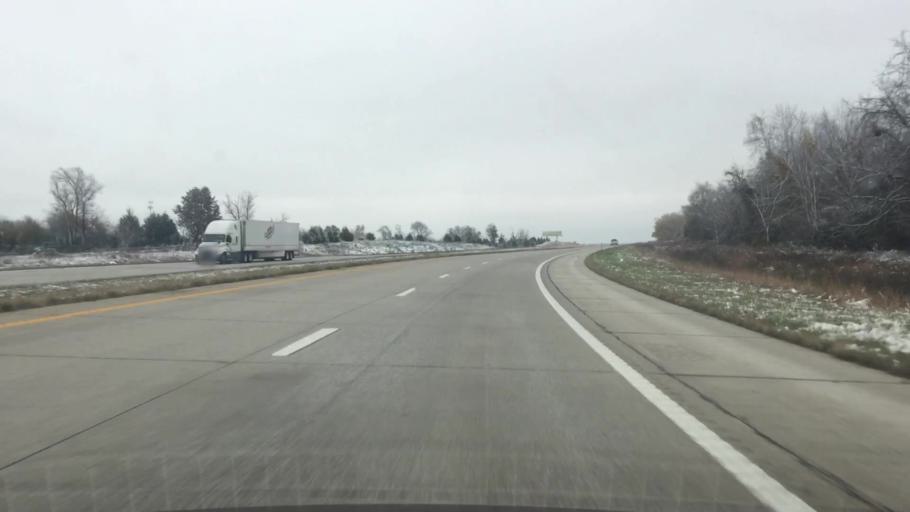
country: US
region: Missouri
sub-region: Saint Clair County
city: Osceola
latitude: 38.1745
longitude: -93.7221
